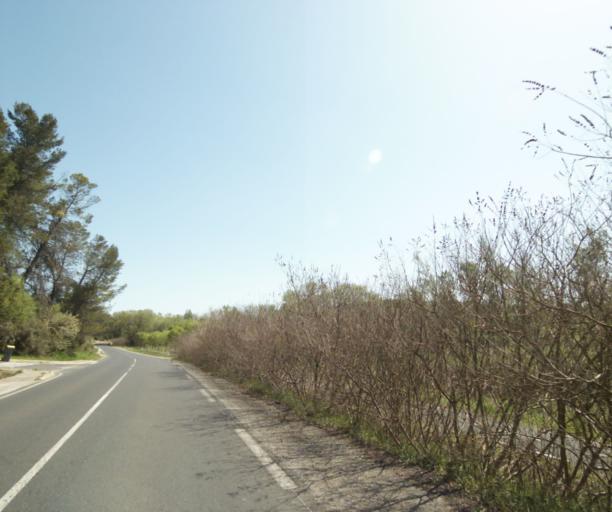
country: FR
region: Languedoc-Roussillon
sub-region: Departement de l'Herault
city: Montferrier-sur-Lez
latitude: 43.6564
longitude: 3.8527
